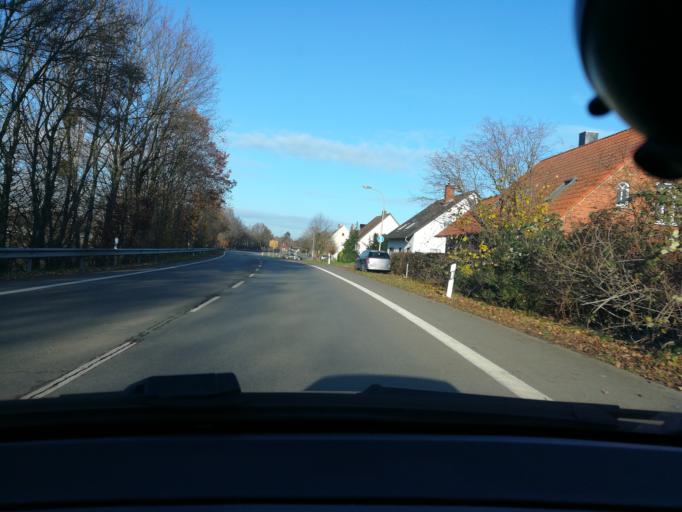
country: DE
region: North Rhine-Westphalia
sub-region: Regierungsbezirk Detmold
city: Petershagen
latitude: 52.3300
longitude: 8.9525
